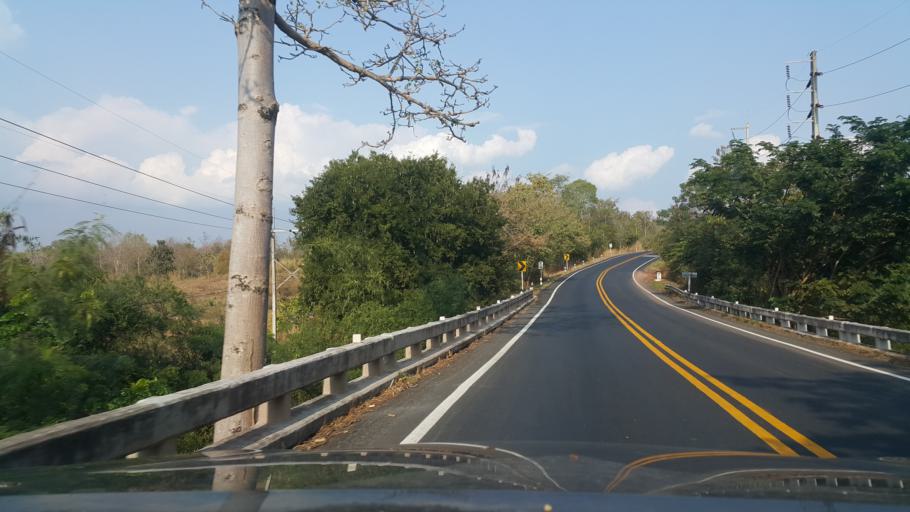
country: TH
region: Phitsanulok
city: Nakhon Thai
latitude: 17.1582
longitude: 100.9618
